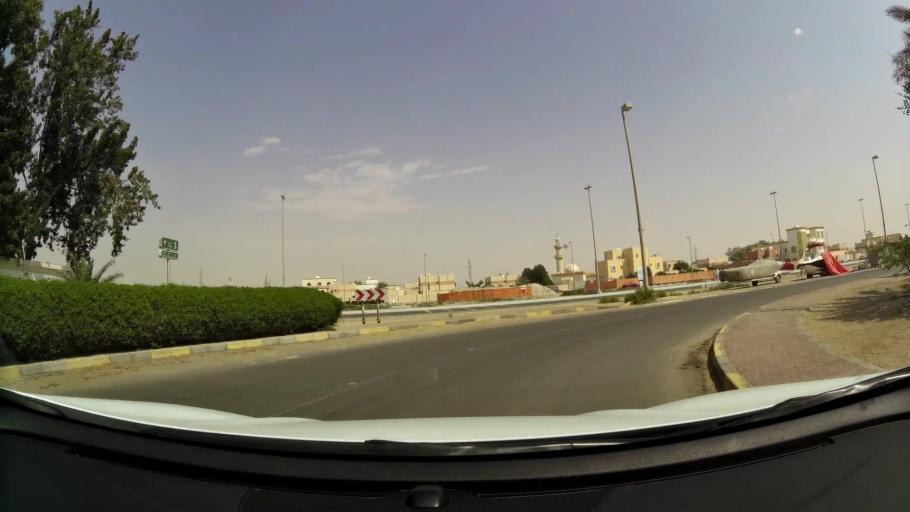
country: AE
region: Abu Dhabi
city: Abu Dhabi
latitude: 24.3055
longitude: 54.6399
